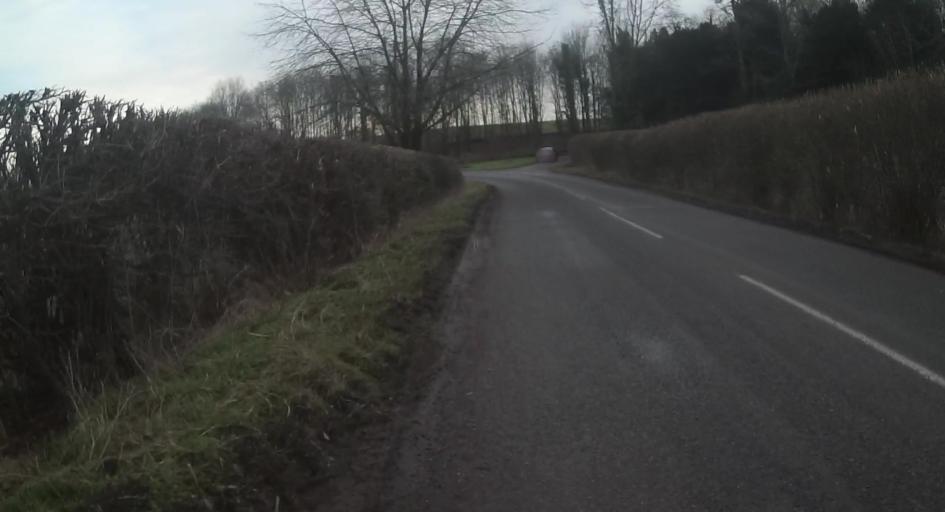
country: GB
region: England
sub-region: Hampshire
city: Highclere
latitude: 51.2228
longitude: -1.3782
